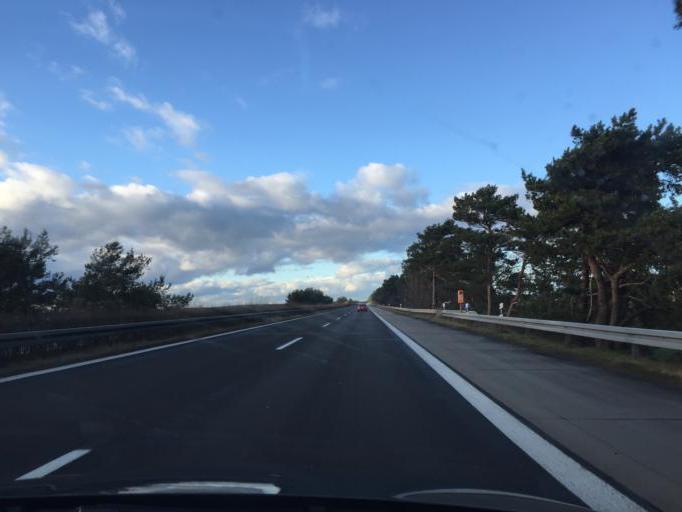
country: DE
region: Brandenburg
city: Vetschau
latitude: 51.8027
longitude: 14.0415
